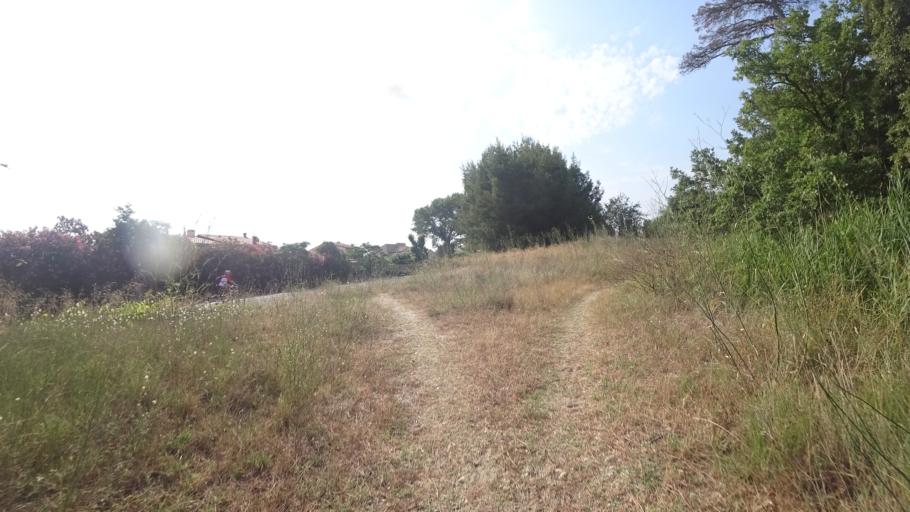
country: FR
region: Languedoc-Roussillon
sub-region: Departement des Pyrenees-Orientales
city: Canet-en-Roussillon
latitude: 42.6885
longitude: 3.0283
